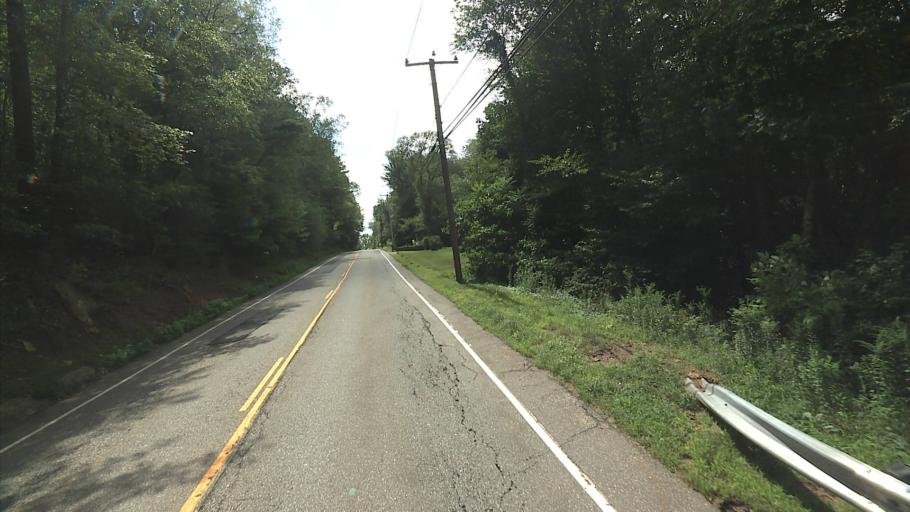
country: US
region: Massachusetts
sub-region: Hampden County
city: Holland
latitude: 41.9818
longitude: -72.1761
